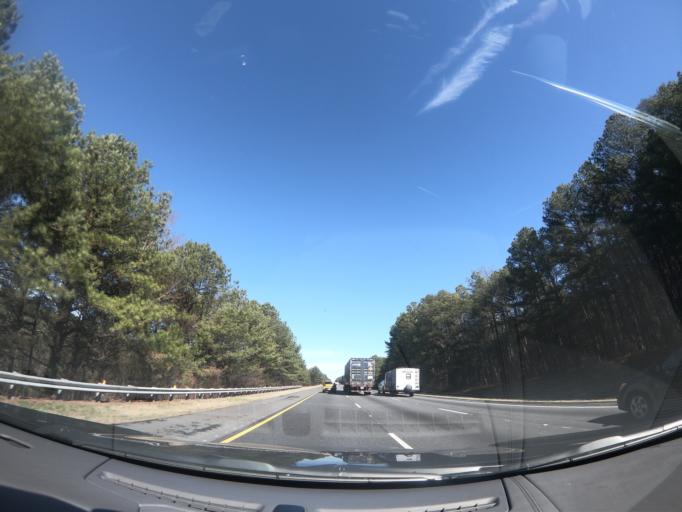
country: US
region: Georgia
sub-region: Whitfield County
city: Dalton
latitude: 34.8239
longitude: -85.0171
